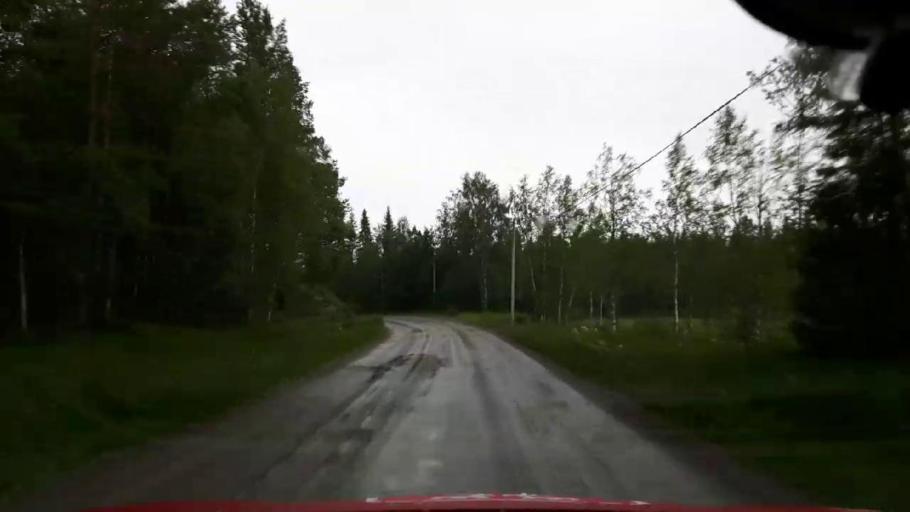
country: SE
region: Jaemtland
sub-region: OEstersunds Kommun
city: Brunflo
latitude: 62.8988
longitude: 14.8641
